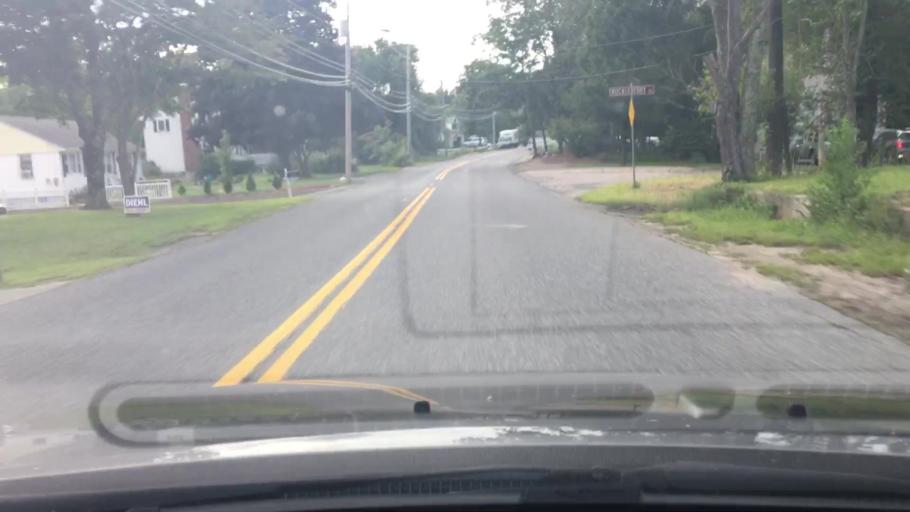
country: US
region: Massachusetts
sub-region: Worcester County
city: Milford
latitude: 42.1760
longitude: -71.5333
